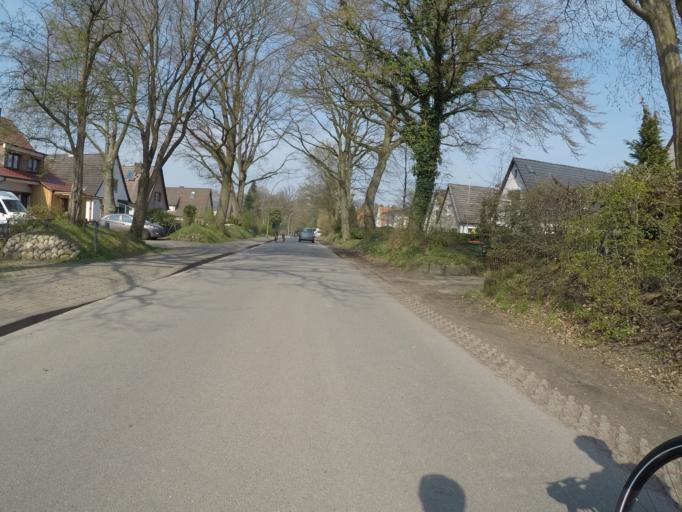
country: DE
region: Hamburg
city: Sasel
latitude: 53.6669
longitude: 10.1063
